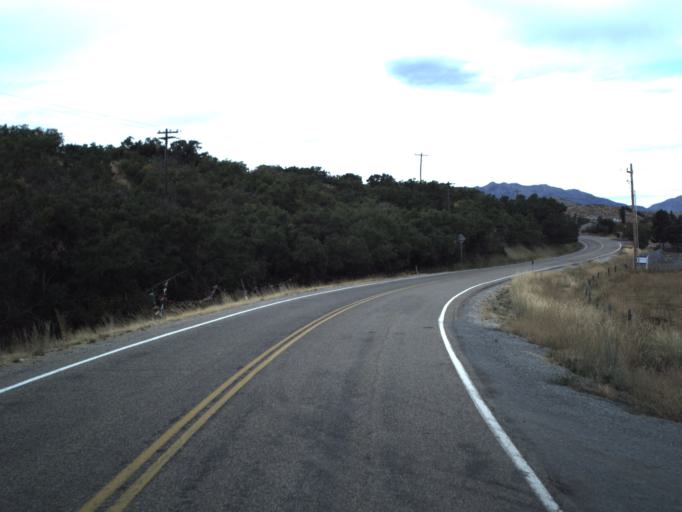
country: US
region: Utah
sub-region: Morgan County
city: Morgan
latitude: 40.9518
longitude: -111.6610
